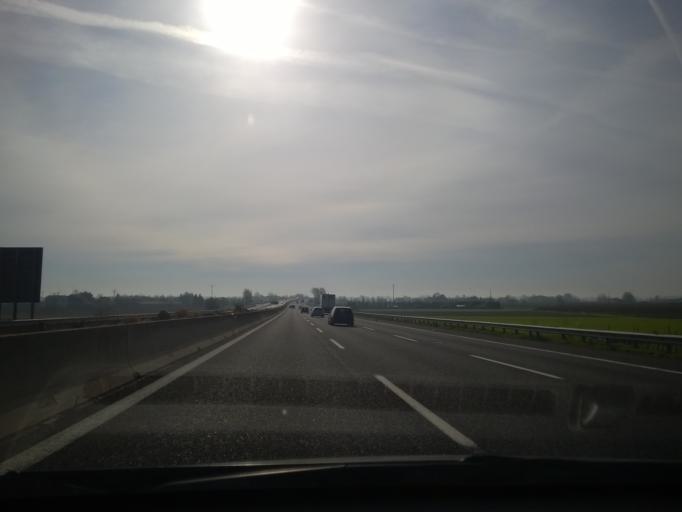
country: IT
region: Emilia-Romagna
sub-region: Provincia di Ravenna
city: Solarolo
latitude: 44.3492
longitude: 11.8308
